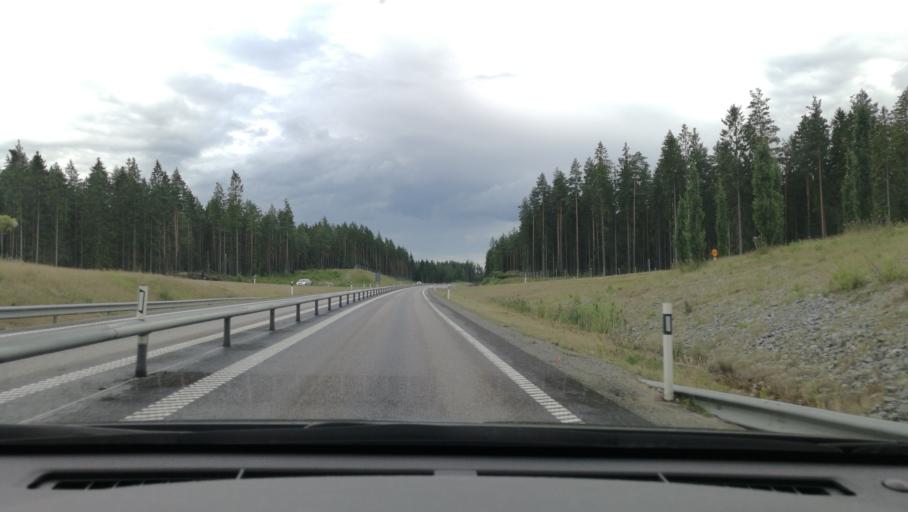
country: SE
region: Soedermanland
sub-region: Katrineholms Kommun
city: Katrineholm
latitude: 58.9938
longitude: 16.2598
